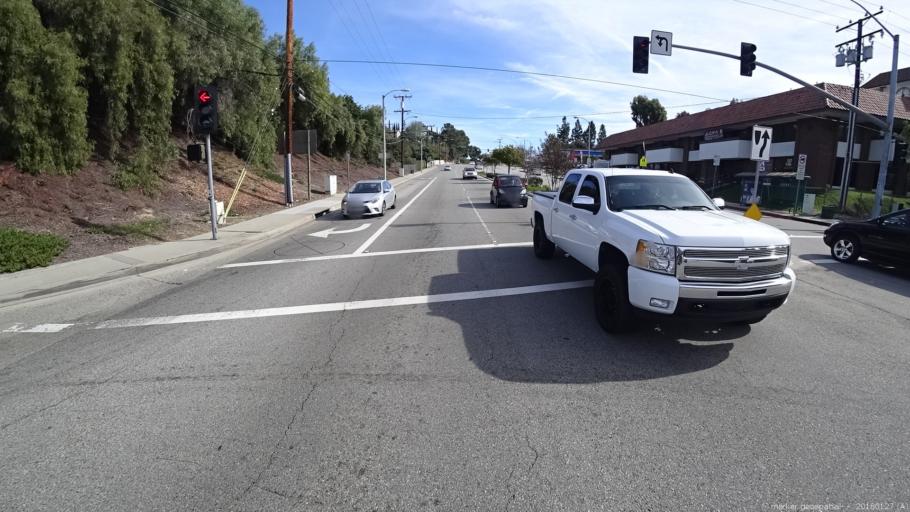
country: US
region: California
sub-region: Los Angeles County
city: Walnut
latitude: 33.9843
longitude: -117.8418
